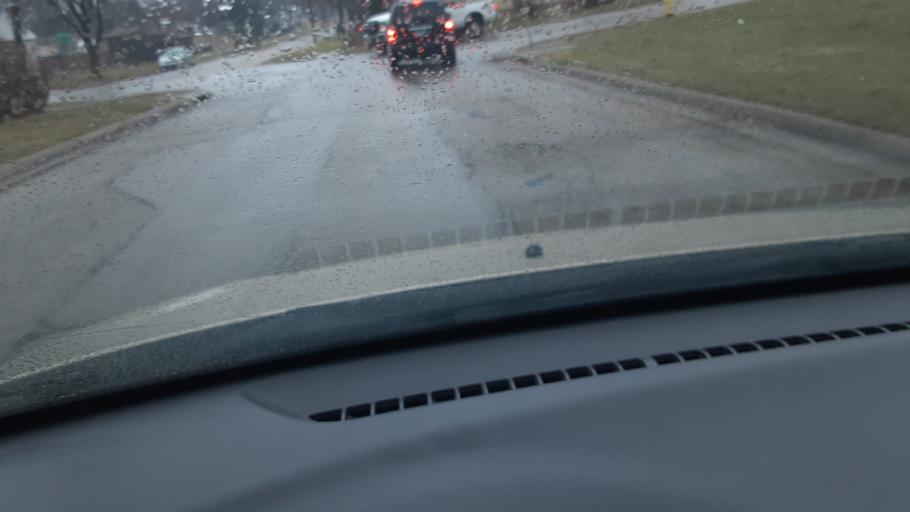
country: US
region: Illinois
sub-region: Winnebago County
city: Rockford
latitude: 42.2853
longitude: -89.1165
